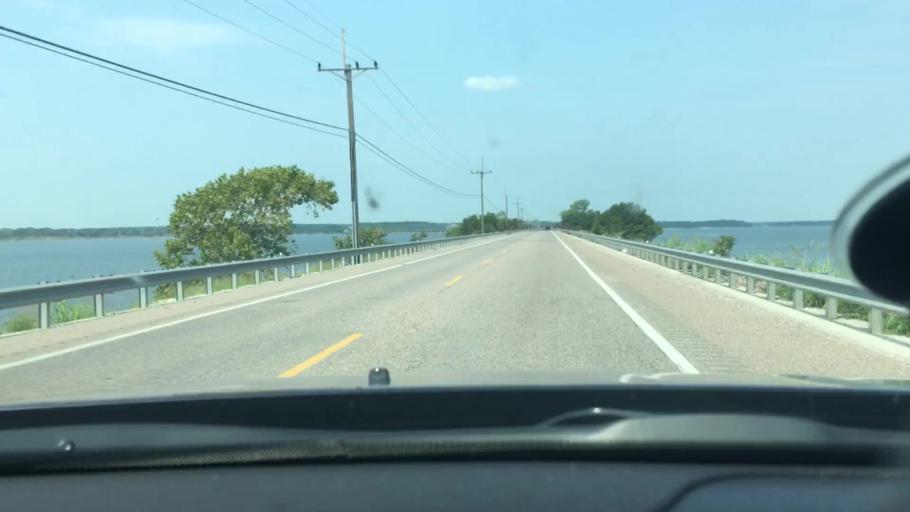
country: US
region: Oklahoma
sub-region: Marshall County
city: Kingston
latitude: 34.0006
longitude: -96.6019
